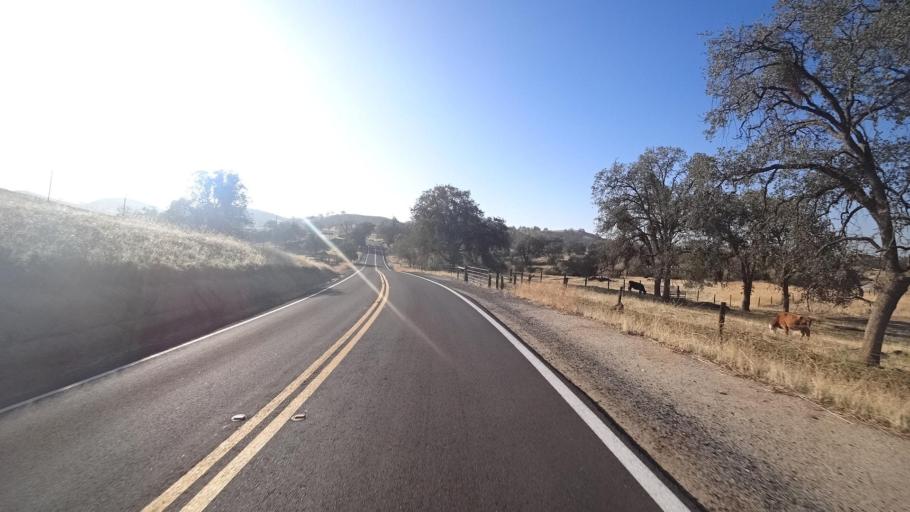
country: US
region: California
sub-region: Tulare County
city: Richgrove
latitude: 35.7332
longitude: -118.8599
